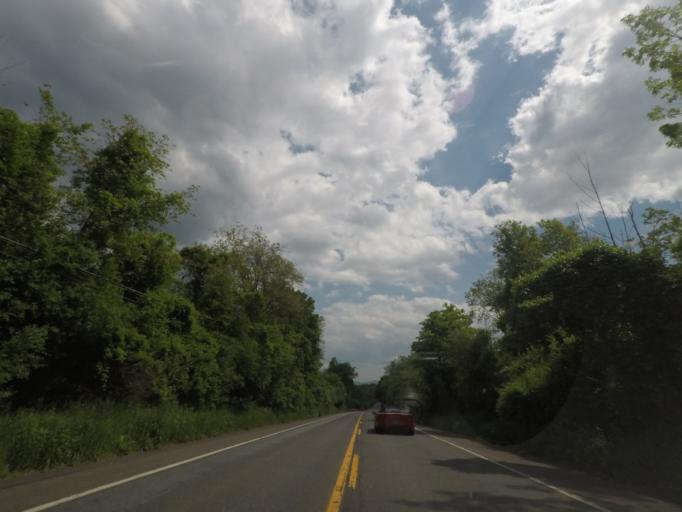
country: US
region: New York
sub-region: Dutchess County
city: Dover Plains
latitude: 41.8866
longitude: -73.5293
